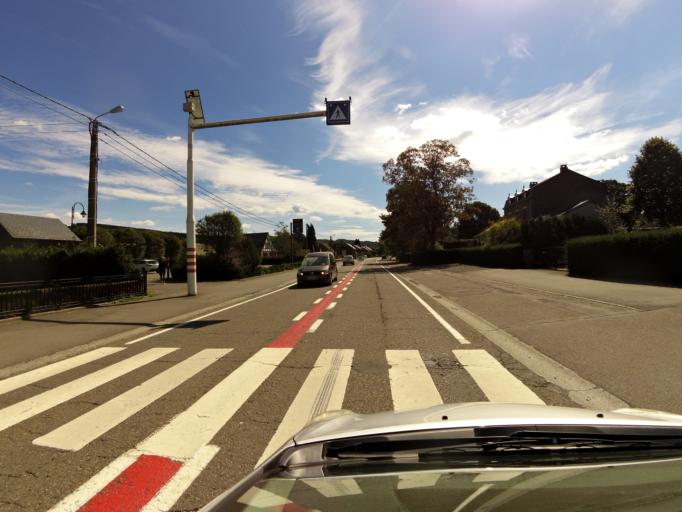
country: BE
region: Wallonia
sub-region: Province du Luxembourg
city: Rendeux
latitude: 50.2403
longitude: 5.5019
